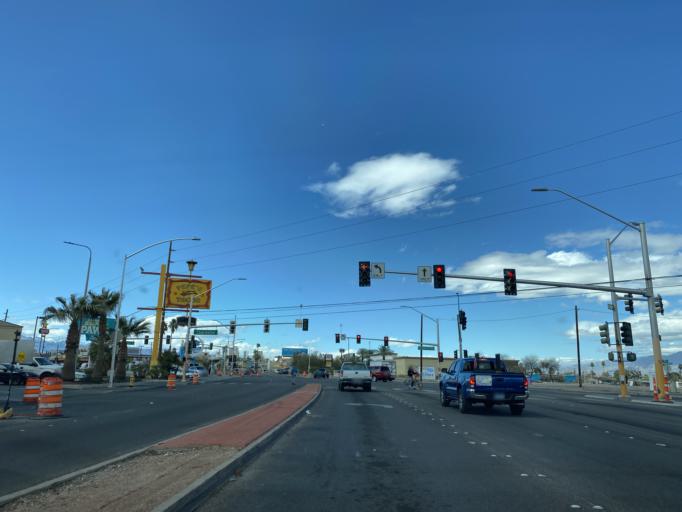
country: US
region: Nevada
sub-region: Clark County
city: Las Vegas
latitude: 36.1584
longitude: -115.1160
